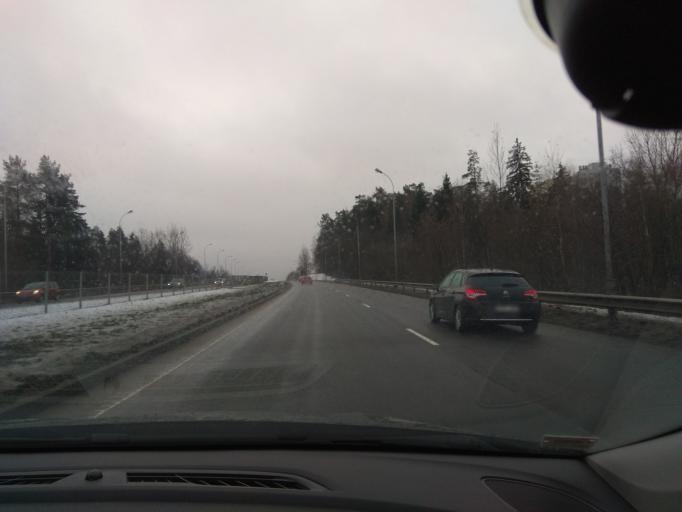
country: LT
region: Vilnius County
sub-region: Vilnius
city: Fabijoniskes
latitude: 54.7352
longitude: 25.2649
